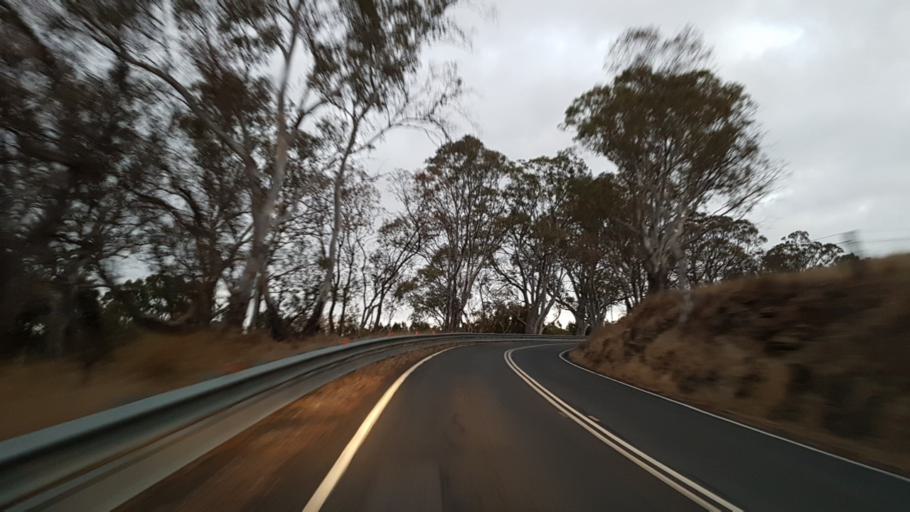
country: AU
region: South Australia
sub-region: Mount Barker
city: Nairne
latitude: -35.0342
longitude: 138.9533
